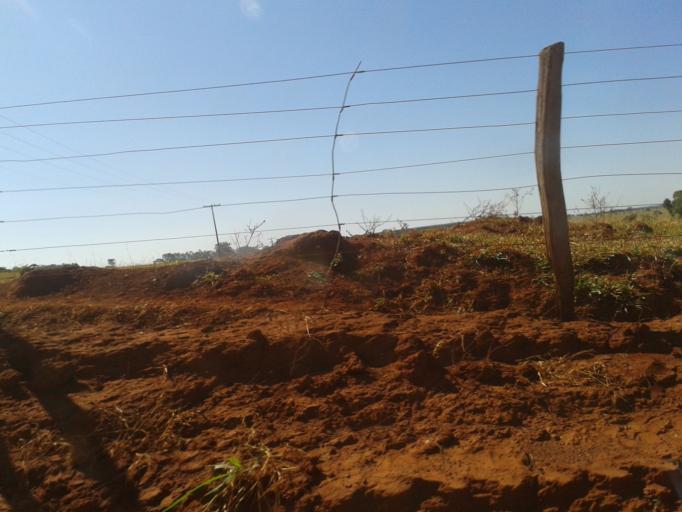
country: BR
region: Minas Gerais
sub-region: Centralina
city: Centralina
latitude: -18.7267
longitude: -49.1787
